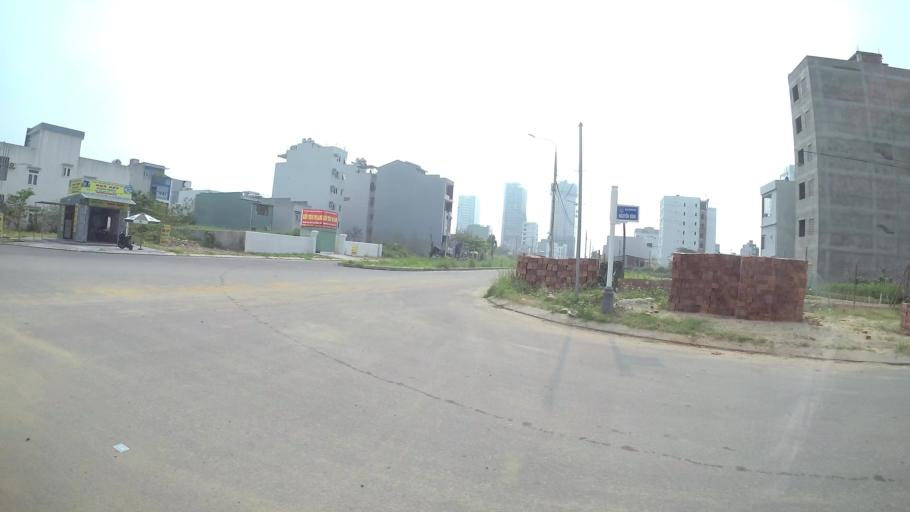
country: VN
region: Da Nang
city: Son Tra
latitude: 16.0813
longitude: 108.2418
